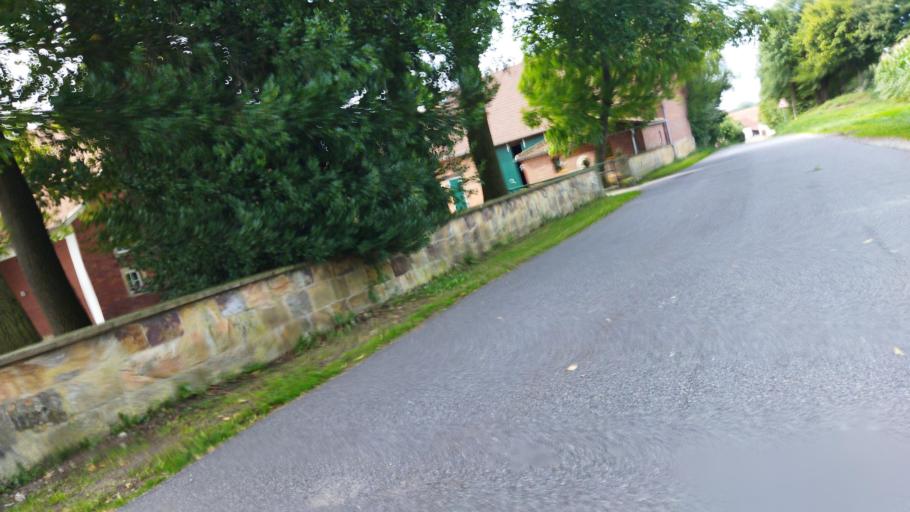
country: DE
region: Lower Saxony
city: Bad Iburg
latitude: 52.1442
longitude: 8.0353
